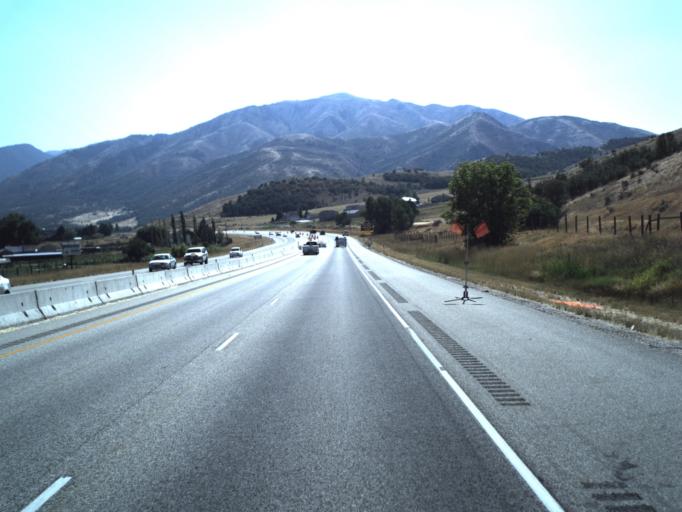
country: US
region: Utah
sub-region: Box Elder County
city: Brigham City
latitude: 41.5137
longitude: -111.9424
